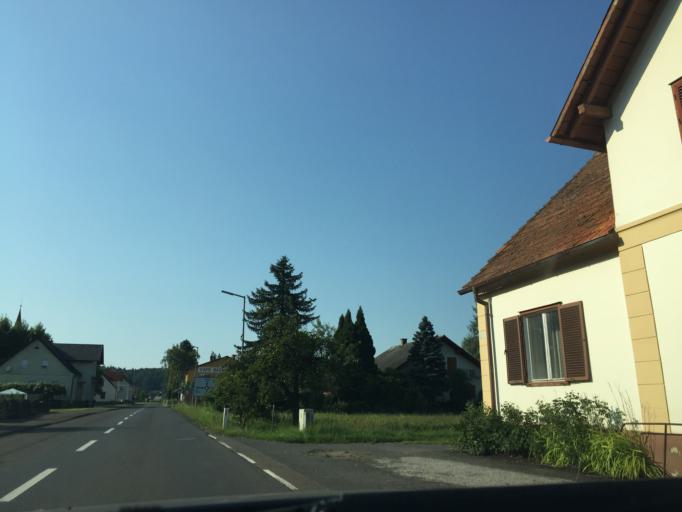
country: AT
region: Styria
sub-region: Politischer Bezirk Suedoststeiermark
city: Deutsch Goritz
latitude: 46.7495
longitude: 15.8316
